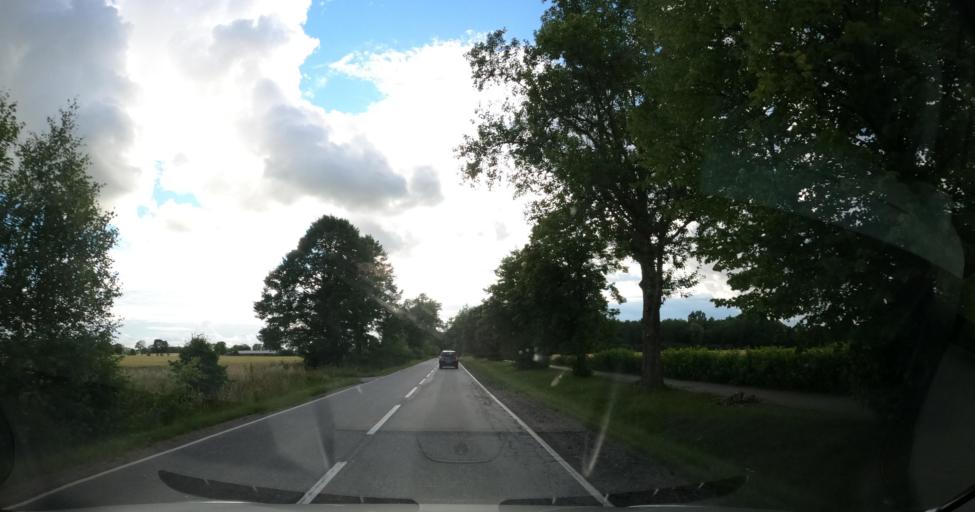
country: PL
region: Pomeranian Voivodeship
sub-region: Powiat slupski
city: Potegowo
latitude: 54.4184
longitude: 17.3955
